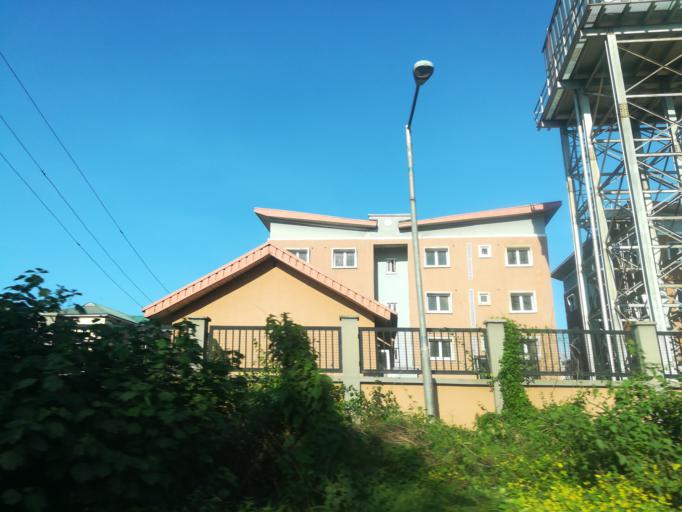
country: NG
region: Lagos
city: Ikorodu
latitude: 6.5631
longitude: 3.5353
